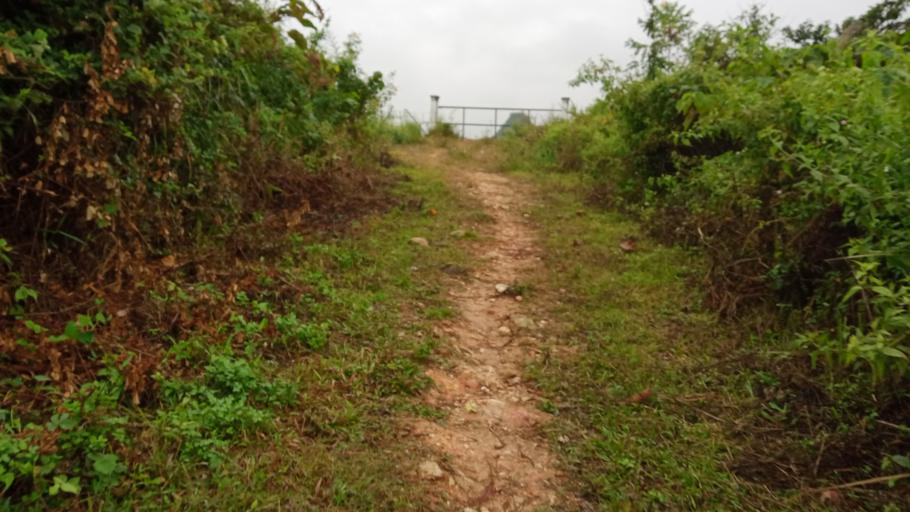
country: LA
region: Xiangkhoang
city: Phonsavan
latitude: 19.1056
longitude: 102.9266
